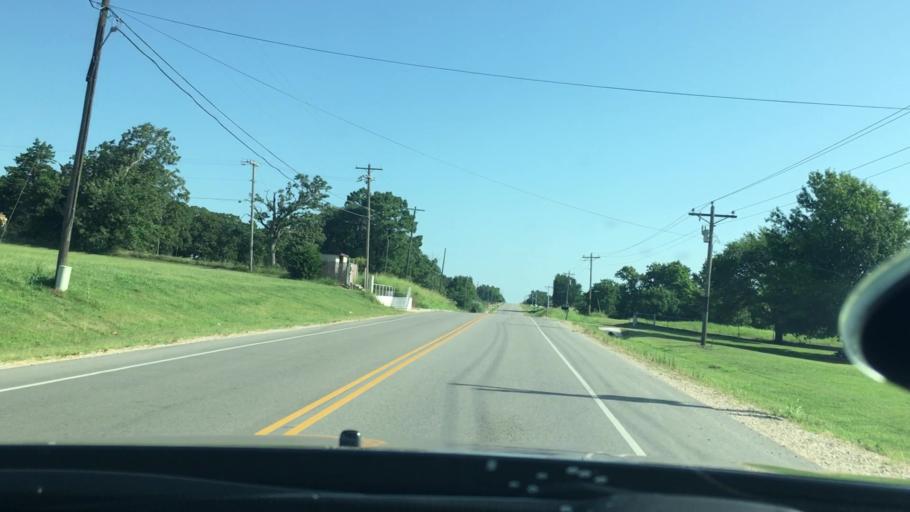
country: US
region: Oklahoma
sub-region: Pontotoc County
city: Ada
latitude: 34.8028
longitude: -96.6523
